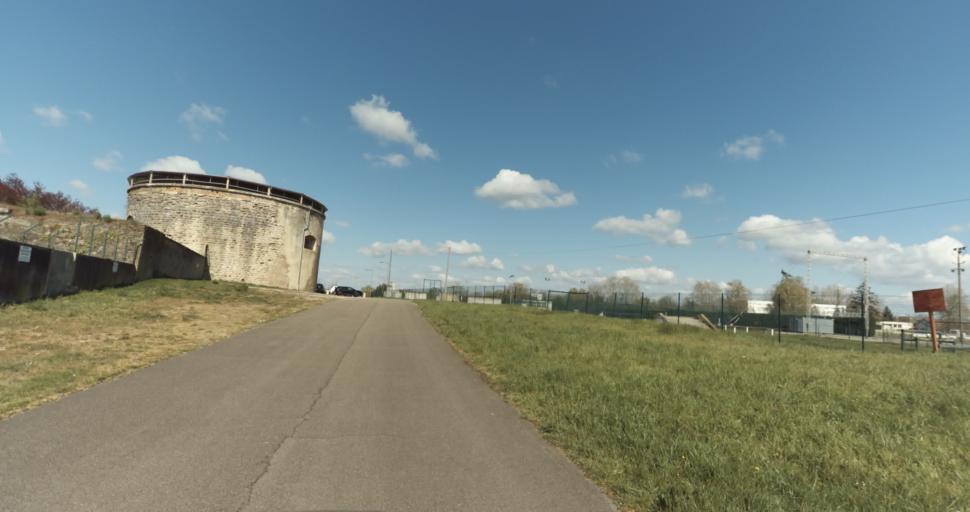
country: FR
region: Bourgogne
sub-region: Departement de la Cote-d'Or
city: Auxonne
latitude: 47.1966
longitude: 5.3925
